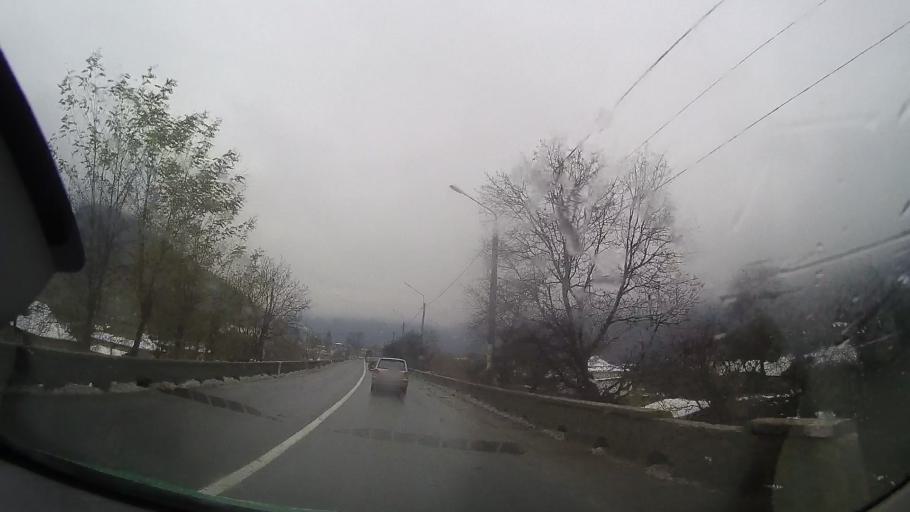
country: RO
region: Neamt
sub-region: Comuna Bicaz
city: Dodeni
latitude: 46.9062
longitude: 26.1075
